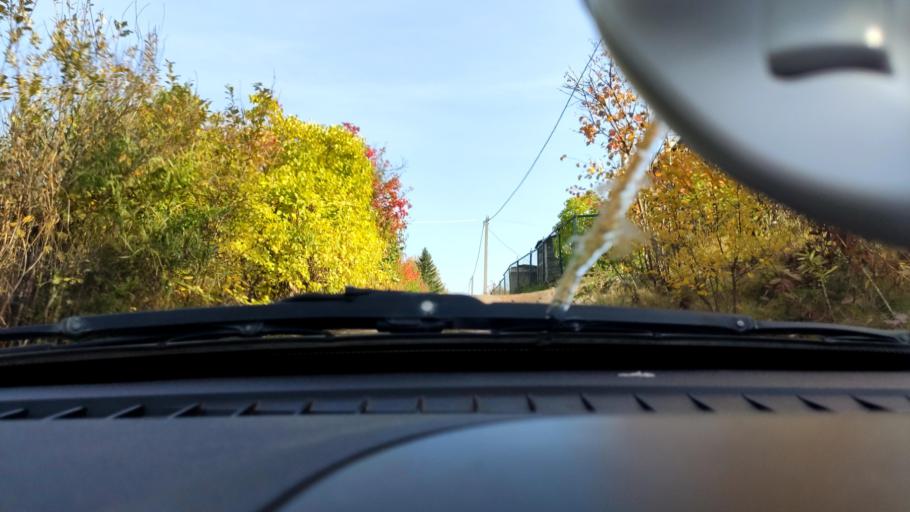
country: RU
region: Perm
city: Overyata
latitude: 58.1036
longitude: 55.8564
